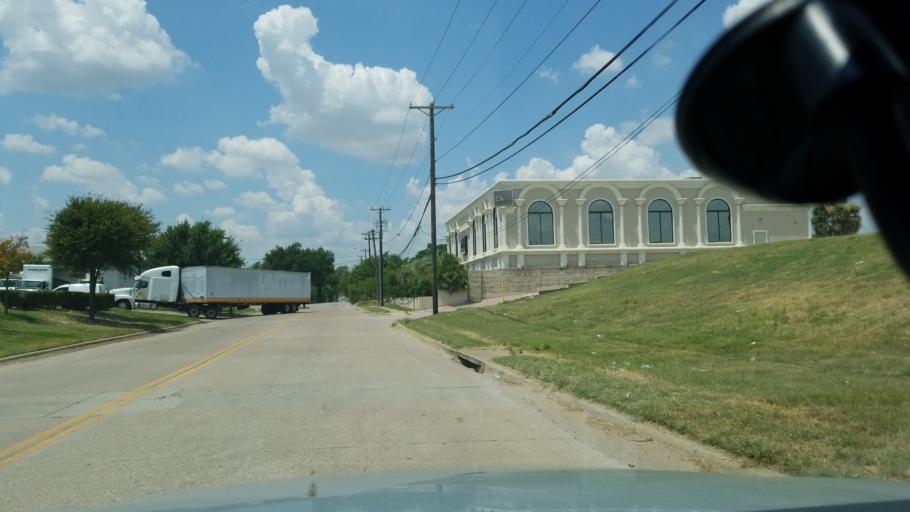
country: US
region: Texas
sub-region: Dallas County
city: Farmers Branch
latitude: 32.8738
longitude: -96.9069
